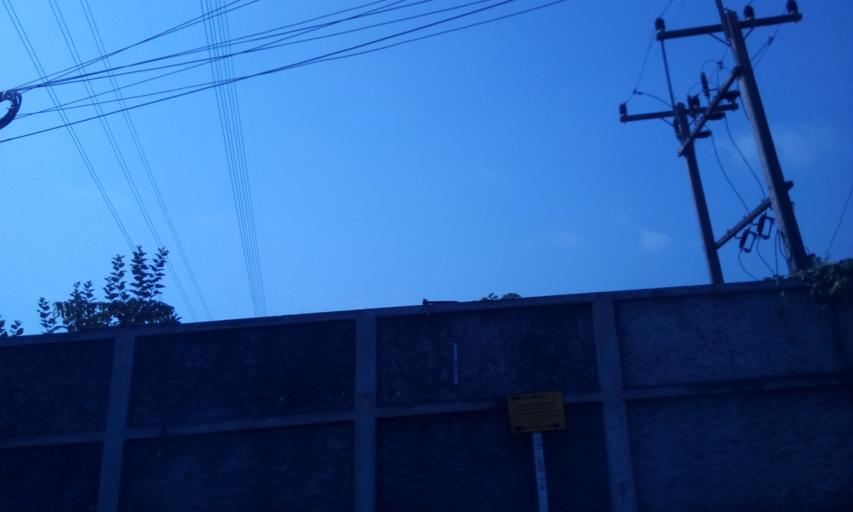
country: TH
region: Pathum Thani
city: Lam Luk Ka
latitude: 13.9333
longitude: 100.7004
